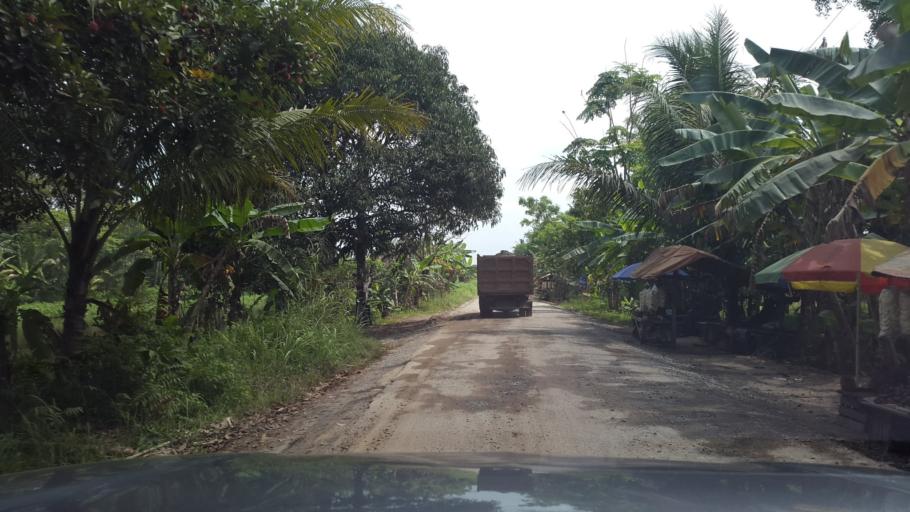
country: ID
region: South Sumatra
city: Tanjung Lubuk
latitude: -3.2661
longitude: 104.8693
